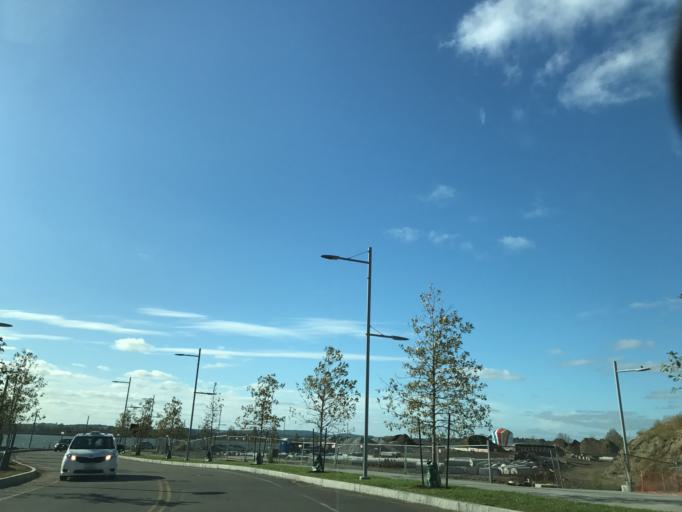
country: US
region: Massachusetts
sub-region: Suffolk County
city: South Boston
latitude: 42.3125
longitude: -71.0364
